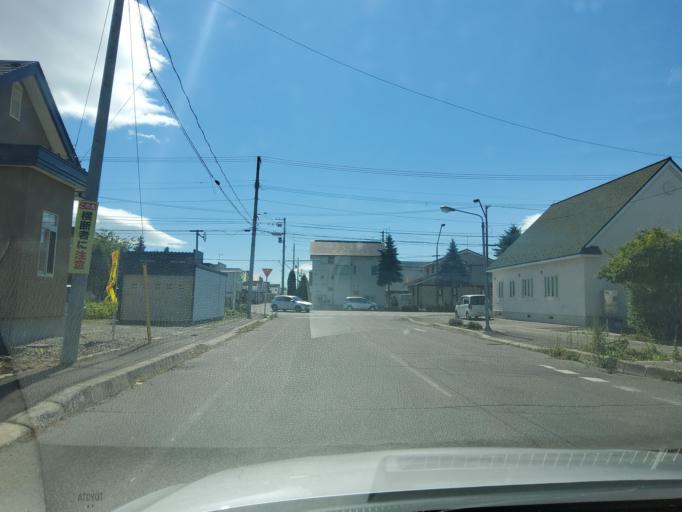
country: JP
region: Hokkaido
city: Otofuke
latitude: 42.9569
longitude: 143.1939
